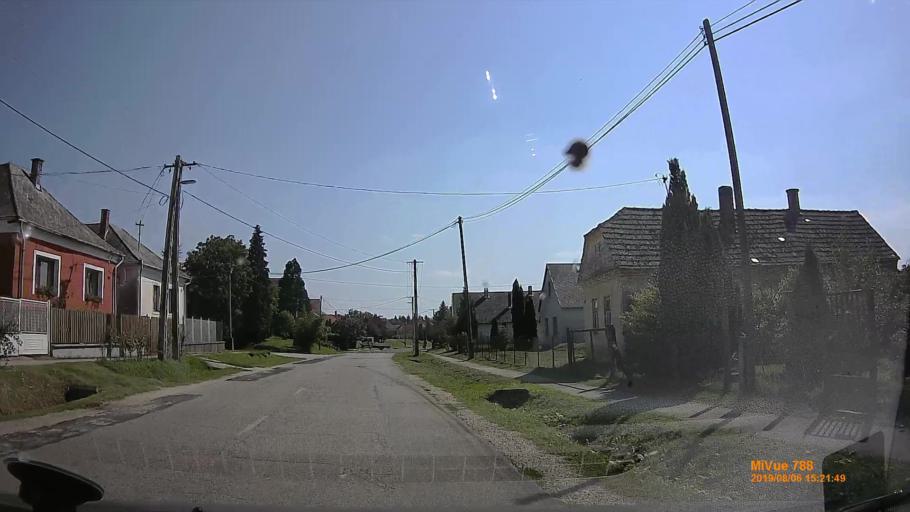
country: HR
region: Koprivnicko-Krizevacka
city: Drnje
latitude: 46.2732
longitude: 16.9488
